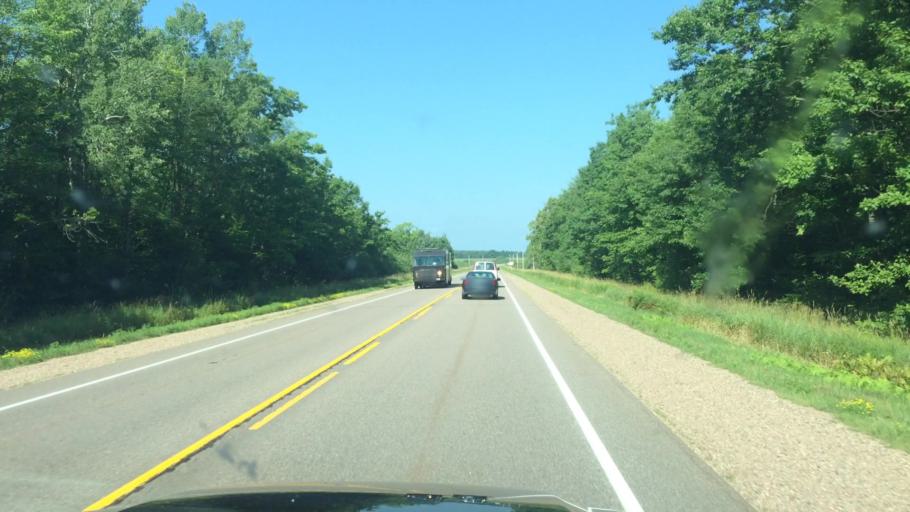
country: US
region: Wisconsin
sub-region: Langlade County
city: Antigo
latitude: 45.1470
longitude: -89.3880
